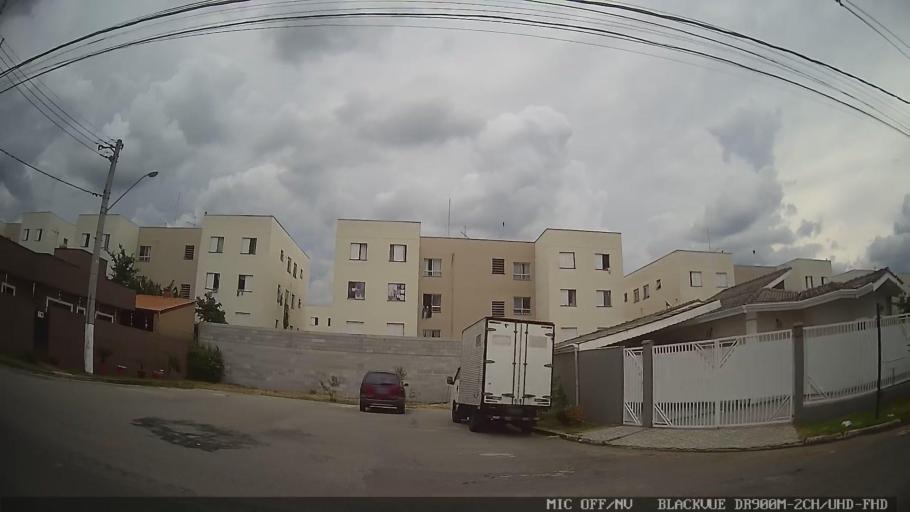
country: BR
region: Sao Paulo
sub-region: Atibaia
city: Atibaia
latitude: -23.1302
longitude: -46.5983
